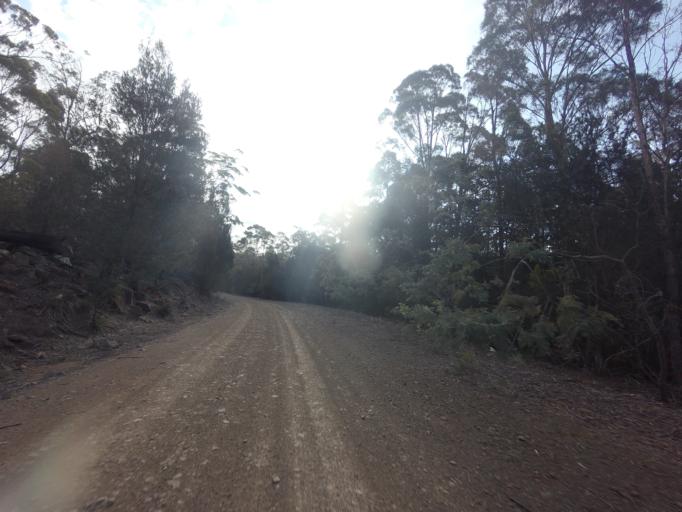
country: AU
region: Tasmania
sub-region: Break O'Day
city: St Helens
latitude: -41.8374
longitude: 148.0633
